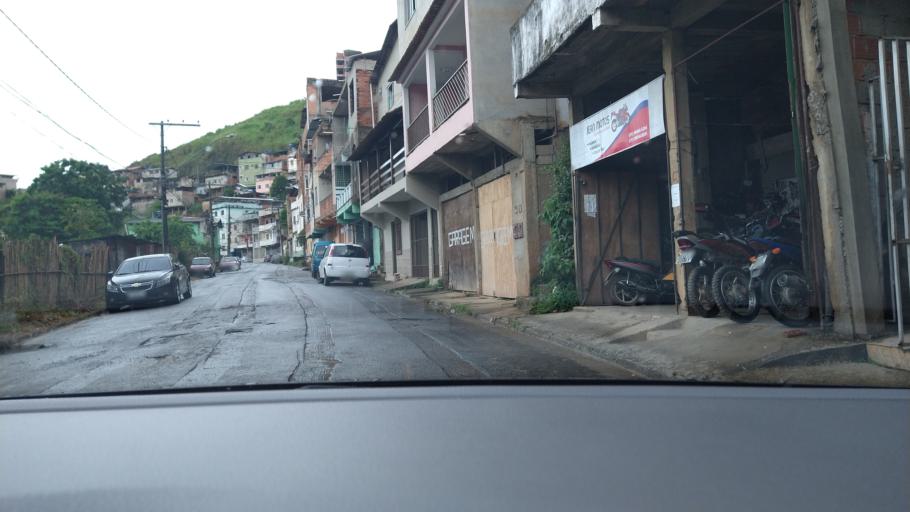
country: BR
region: Minas Gerais
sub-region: Ponte Nova
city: Ponte Nova
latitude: -20.4027
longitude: -42.8974
